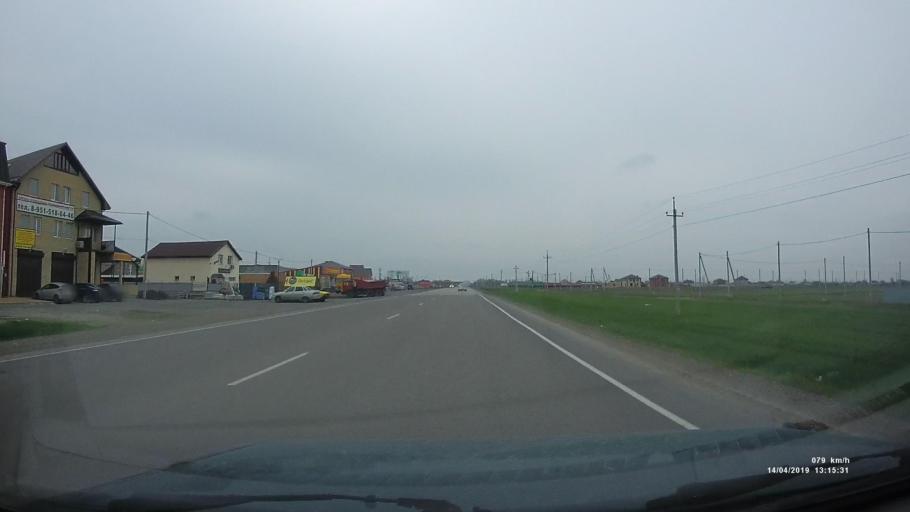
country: RU
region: Rostov
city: Kuleshovka
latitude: 47.0835
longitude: 39.5940
